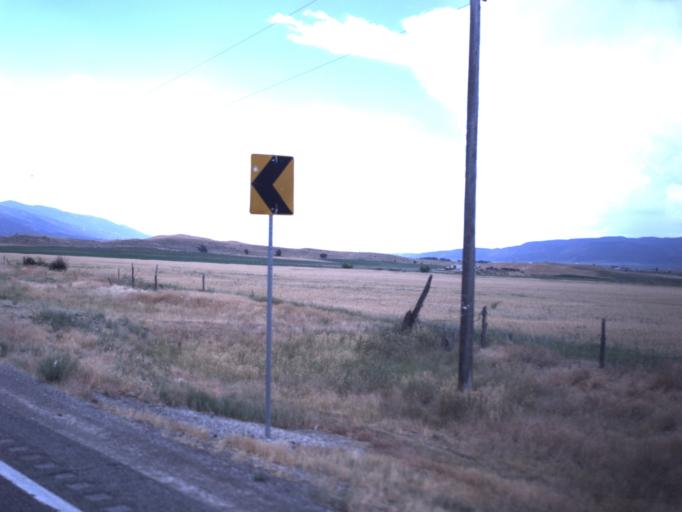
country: US
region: Utah
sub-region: Sanpete County
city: Ephraim
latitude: 39.4242
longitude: -111.5622
